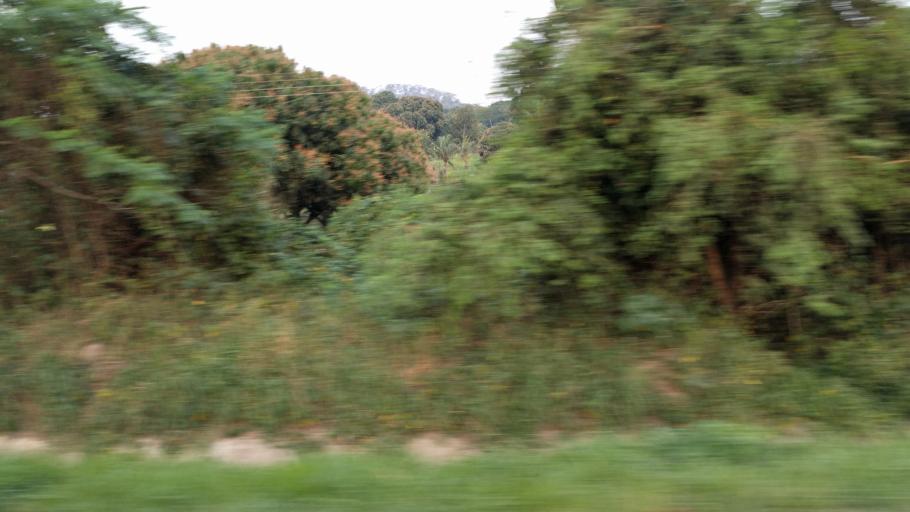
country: BO
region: Santa Cruz
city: Santa Rita
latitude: -17.9530
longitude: -63.3560
